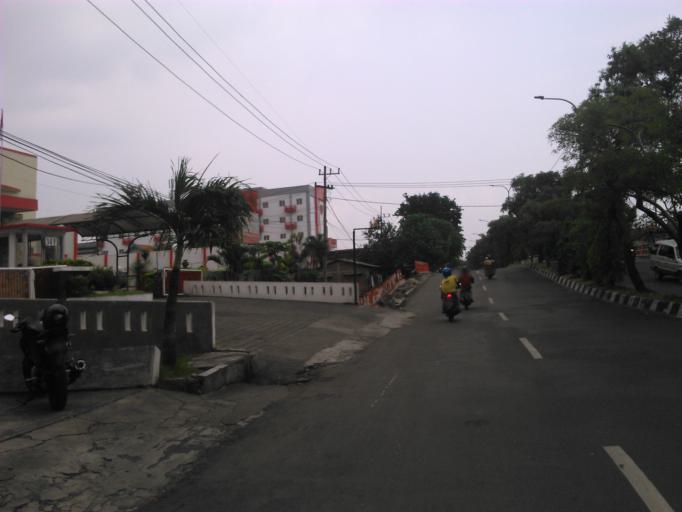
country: ID
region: East Java
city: Gubengairlangga
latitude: -7.2773
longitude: 112.7623
